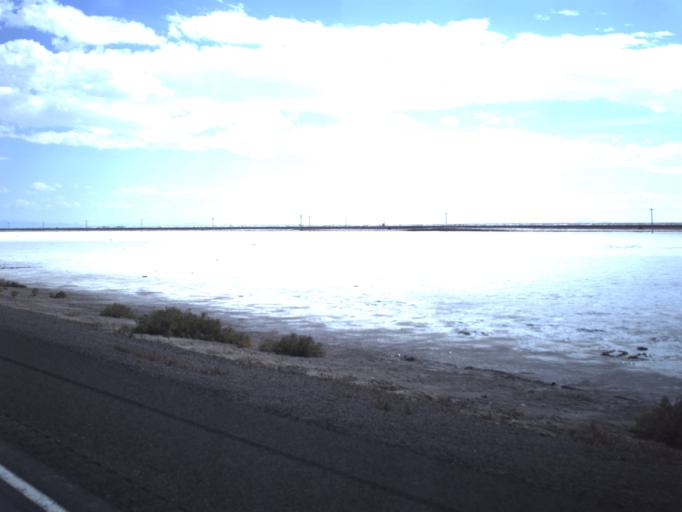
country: US
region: Utah
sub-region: Tooele County
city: Wendover
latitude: 40.7384
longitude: -113.8463
